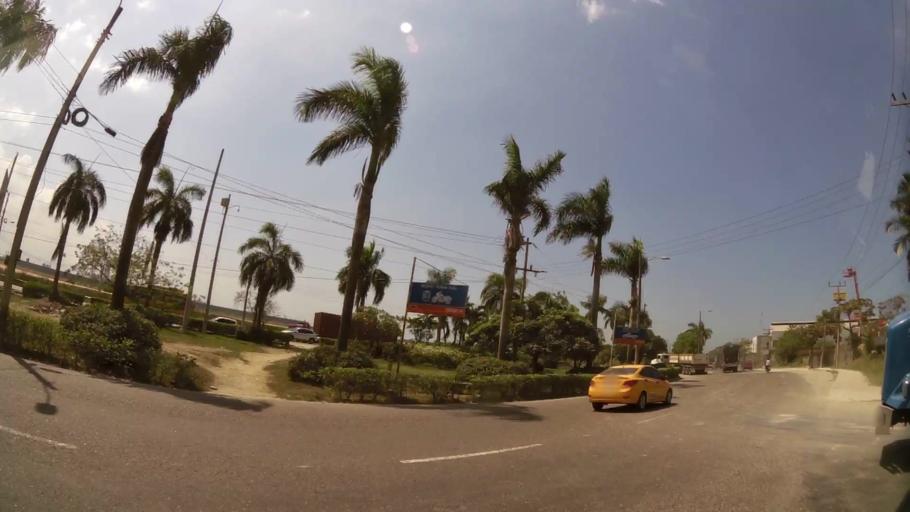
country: CO
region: Bolivar
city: Cartagena
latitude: 10.3549
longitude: -75.4979
